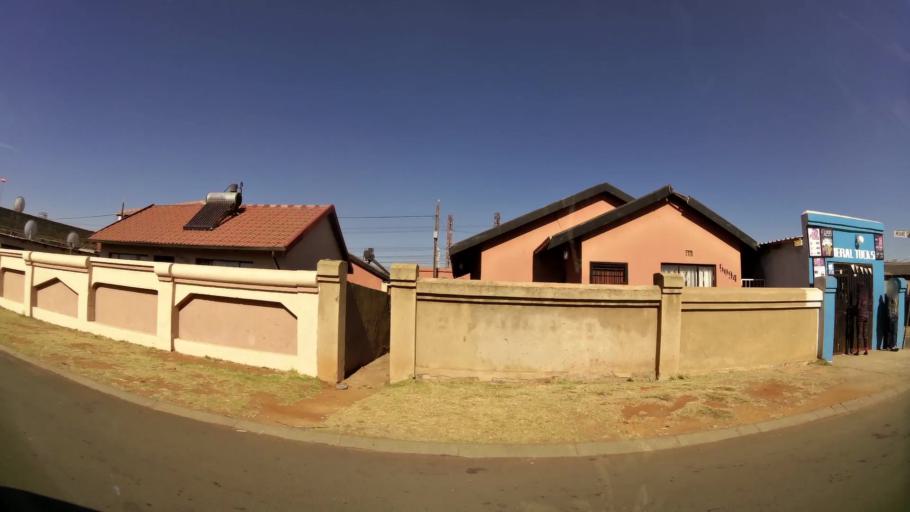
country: ZA
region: Gauteng
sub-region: Ekurhuleni Metropolitan Municipality
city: Tembisa
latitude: -26.0217
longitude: 28.2338
